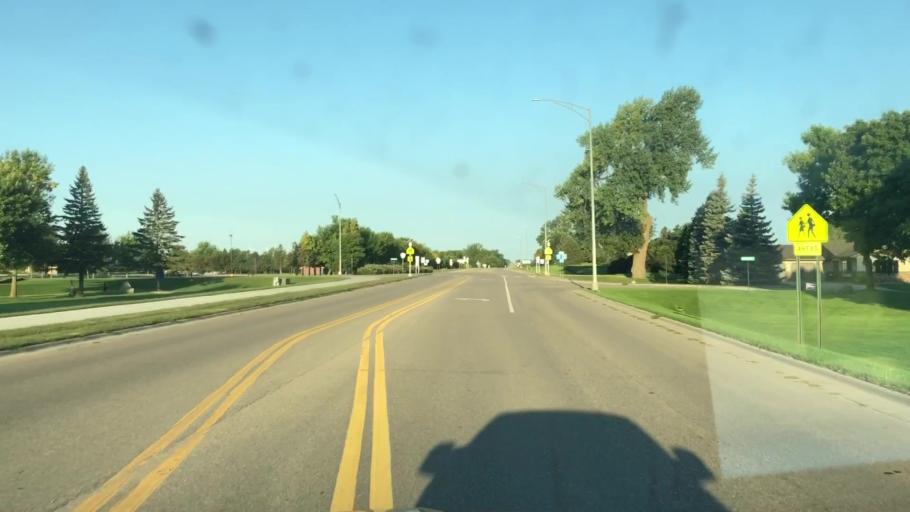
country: US
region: Minnesota
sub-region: Nobles County
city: Worthington
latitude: 43.6310
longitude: -95.6271
